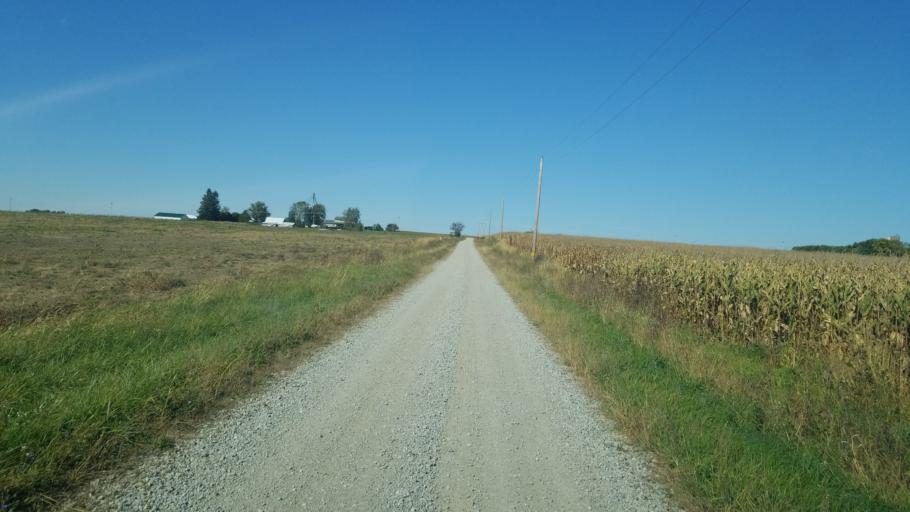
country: US
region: Ohio
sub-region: Huron County
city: New London
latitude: 41.0446
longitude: -82.3459
